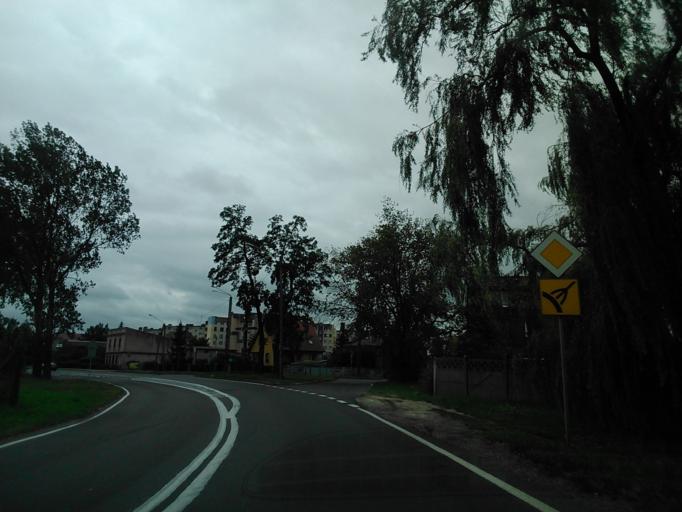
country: PL
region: Kujawsko-Pomorskie
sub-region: Powiat mogilenski
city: Strzelno
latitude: 52.6369
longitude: 18.1718
